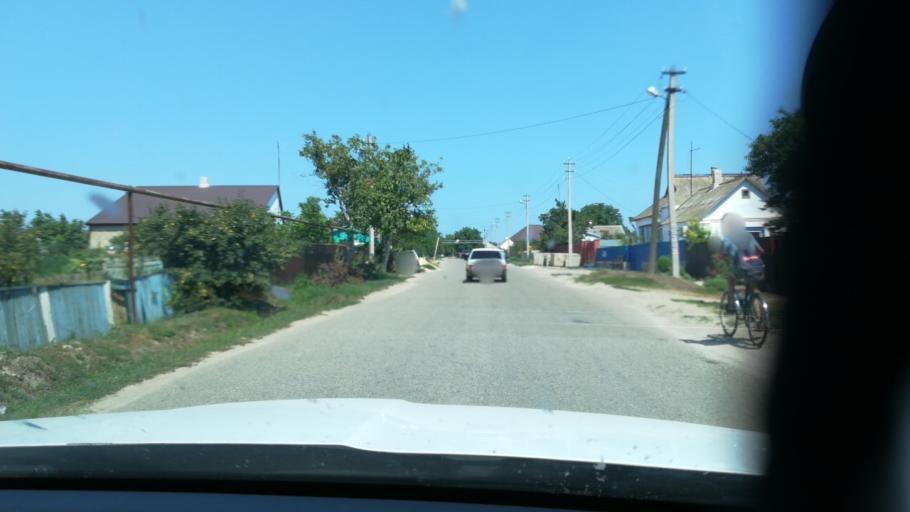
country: RU
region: Krasnodarskiy
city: Starotitarovskaya
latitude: 45.2118
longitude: 37.1445
